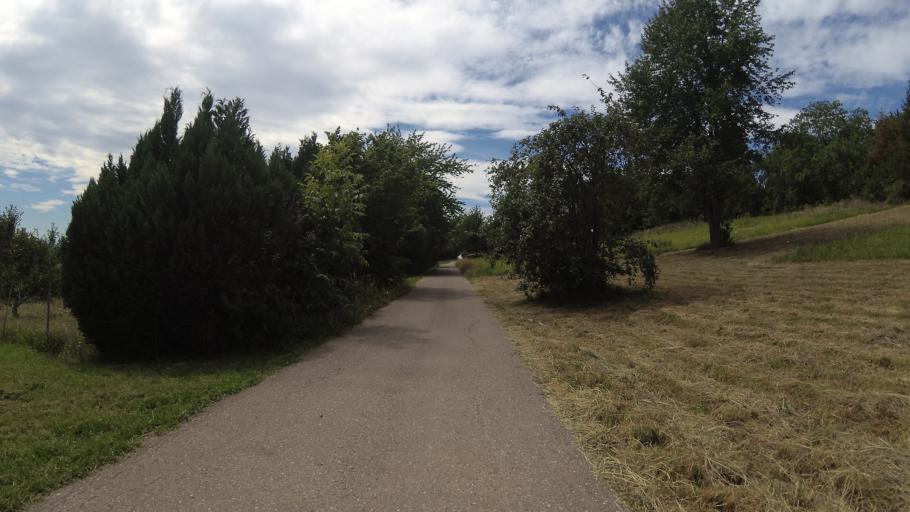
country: DE
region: Baden-Wuerttemberg
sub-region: Regierungsbezirk Stuttgart
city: Neckarsulm
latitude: 49.1921
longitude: 9.2396
